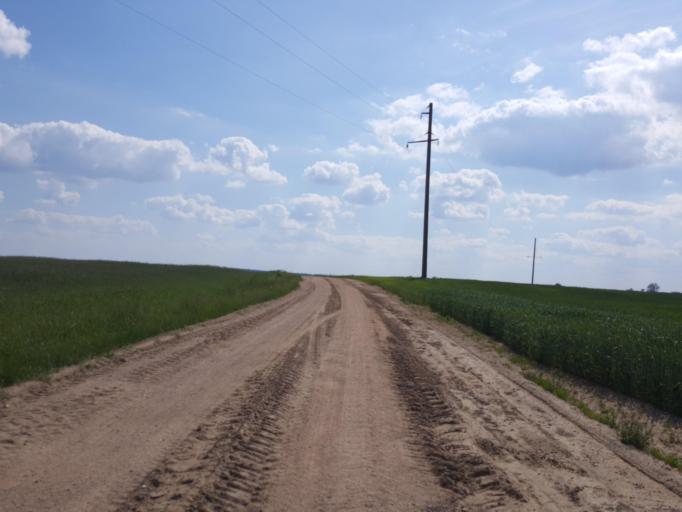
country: BY
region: Brest
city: Kamyanyuki
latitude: 52.4986
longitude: 23.6058
